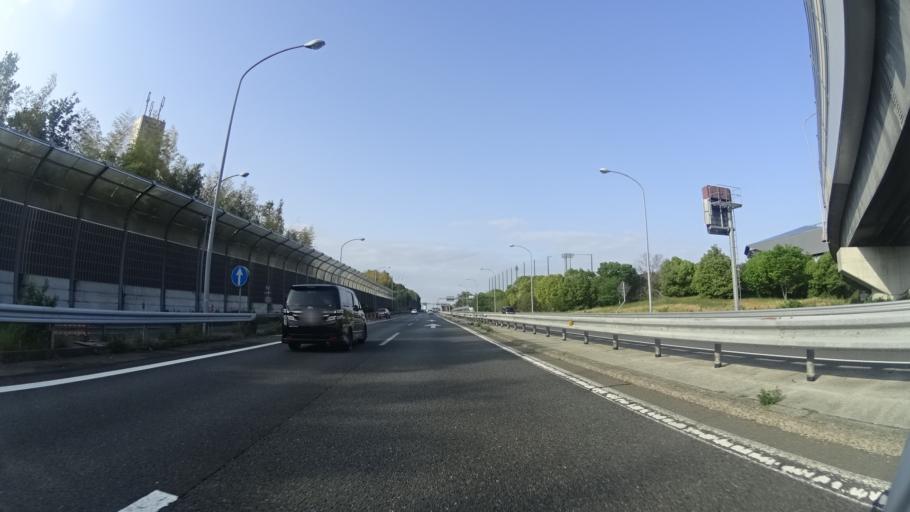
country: JP
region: Osaka
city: Ibaraki
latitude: 34.8031
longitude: 135.5414
